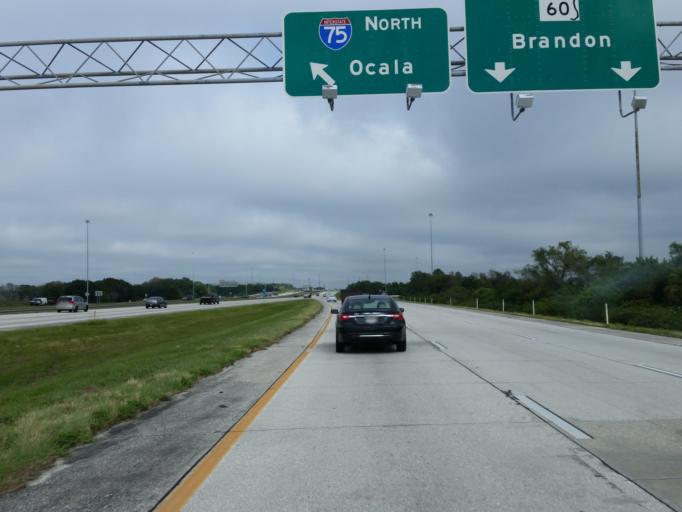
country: US
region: Florida
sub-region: Hillsborough County
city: Brandon
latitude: 27.9327
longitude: -82.3302
